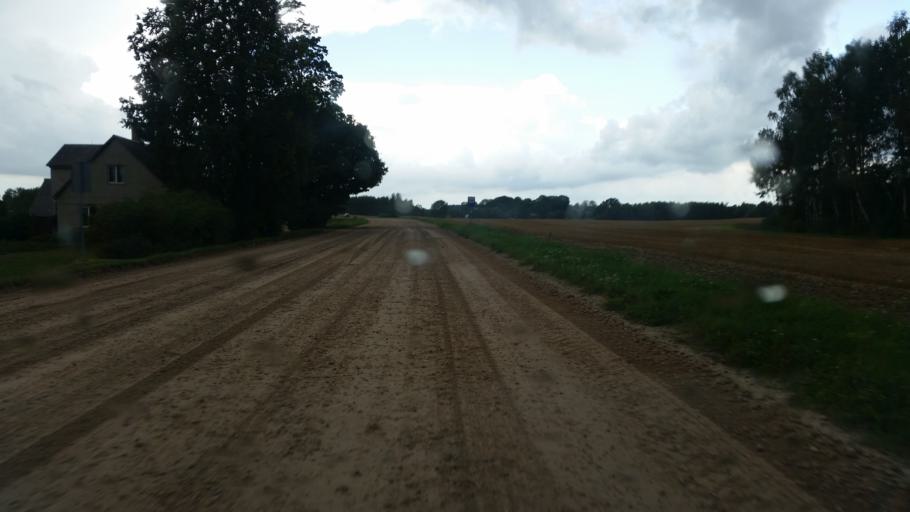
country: LV
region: Vecumnieki
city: Vecumnieki
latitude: 56.4244
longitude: 24.4941
